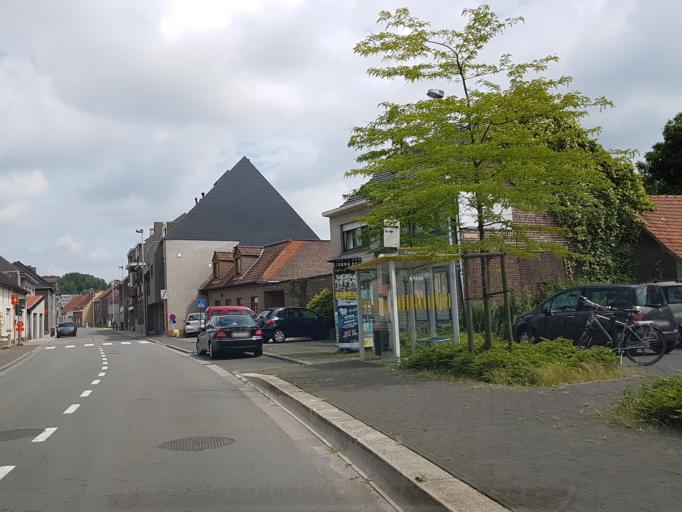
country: BE
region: Flanders
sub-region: Provincie Vlaams-Brabant
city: Liedekerke
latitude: 50.8883
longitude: 4.1001
